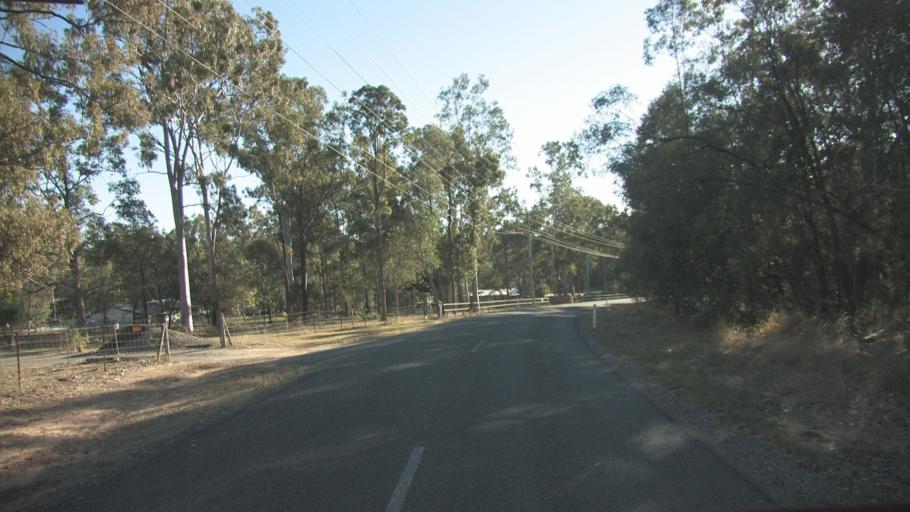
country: AU
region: Queensland
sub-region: Logan
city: North Maclean
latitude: -27.7861
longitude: 152.9620
